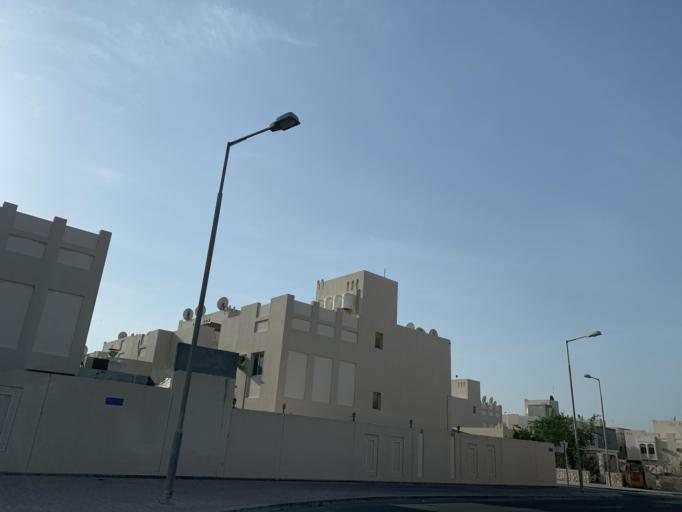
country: BH
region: Central Governorate
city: Madinat Hamad
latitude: 26.1257
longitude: 50.4860
